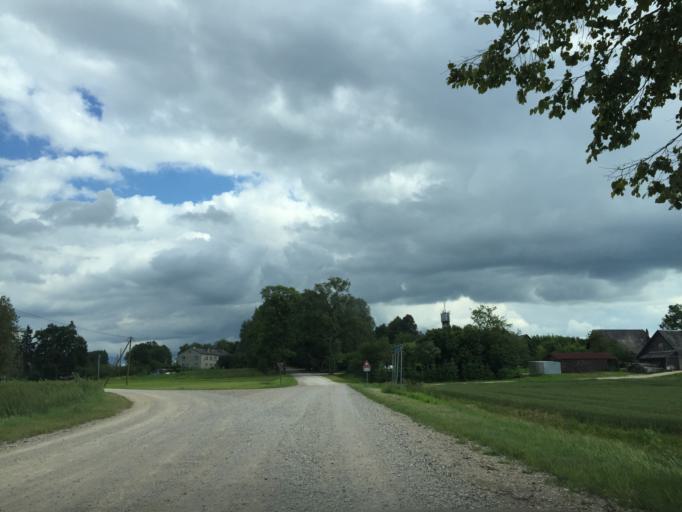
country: LV
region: Malpils
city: Malpils
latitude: 56.8615
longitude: 25.0171
